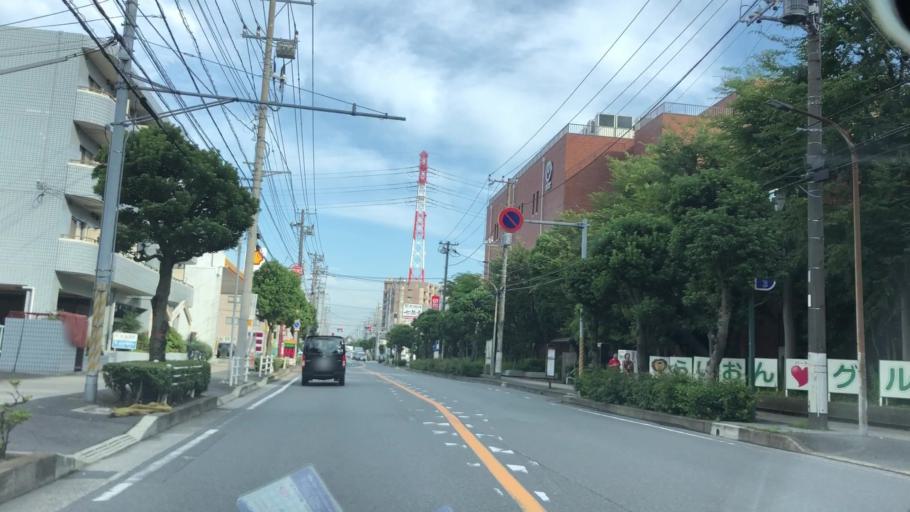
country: JP
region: Tokyo
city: Urayasu
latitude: 35.6796
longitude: 139.9182
